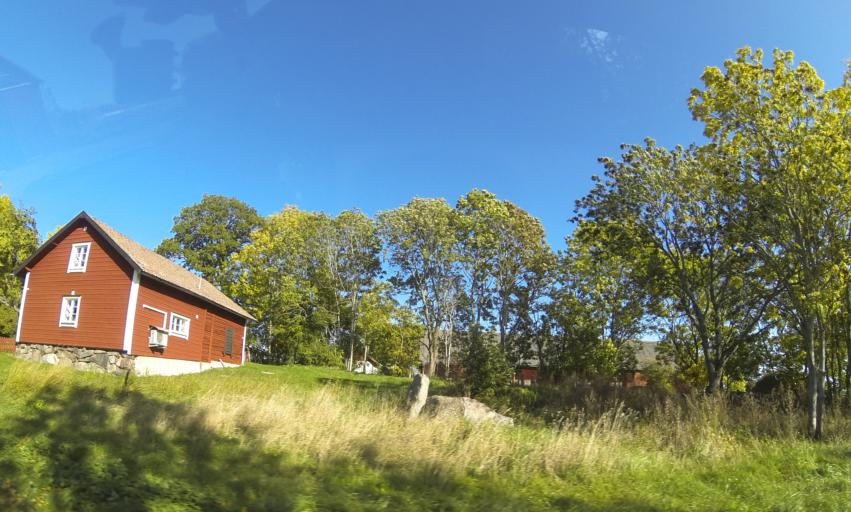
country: SE
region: Vaestmanland
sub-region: Vasteras
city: Vasteras
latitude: 59.5449
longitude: 16.4439
